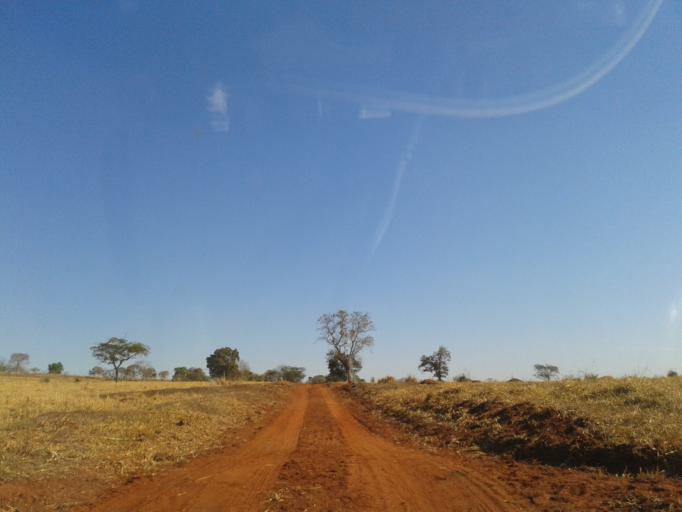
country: BR
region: Minas Gerais
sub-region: Santa Vitoria
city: Santa Vitoria
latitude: -19.0594
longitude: -49.9263
